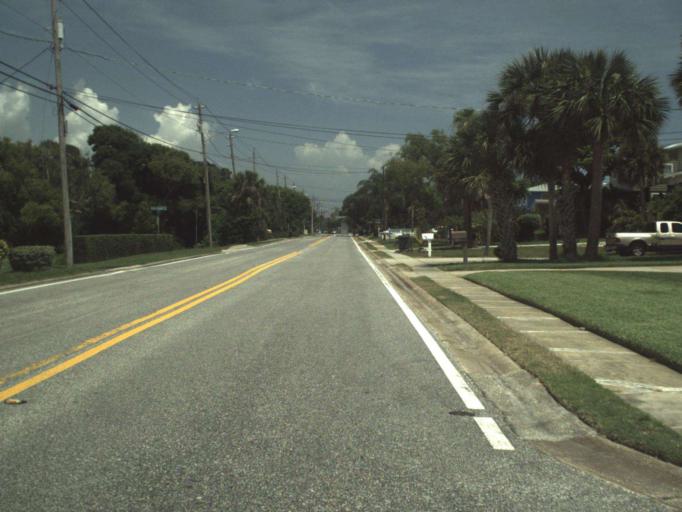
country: US
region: Florida
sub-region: Volusia County
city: Daytona Beach
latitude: 29.2007
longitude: -80.9994
